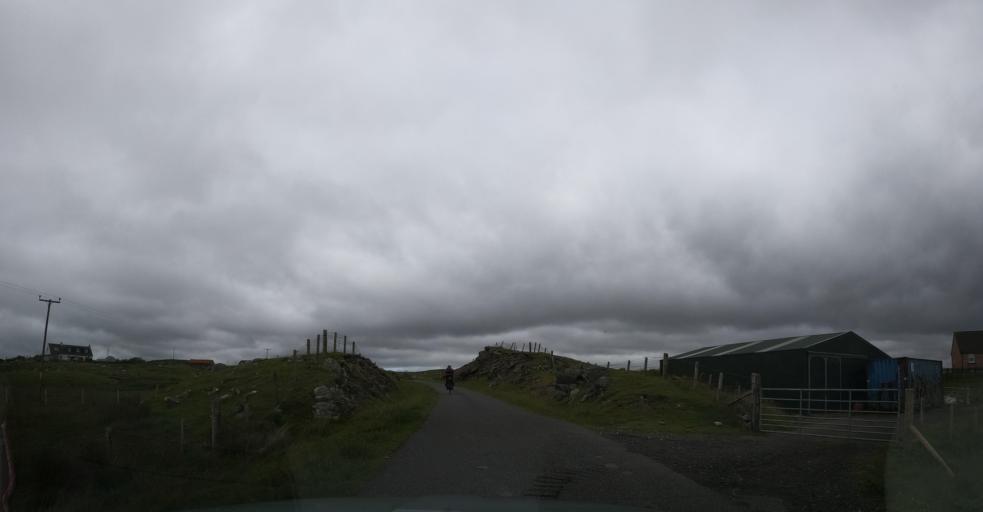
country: GB
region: Scotland
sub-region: Eilean Siar
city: Isle of North Uist
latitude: 57.5440
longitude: -7.3435
